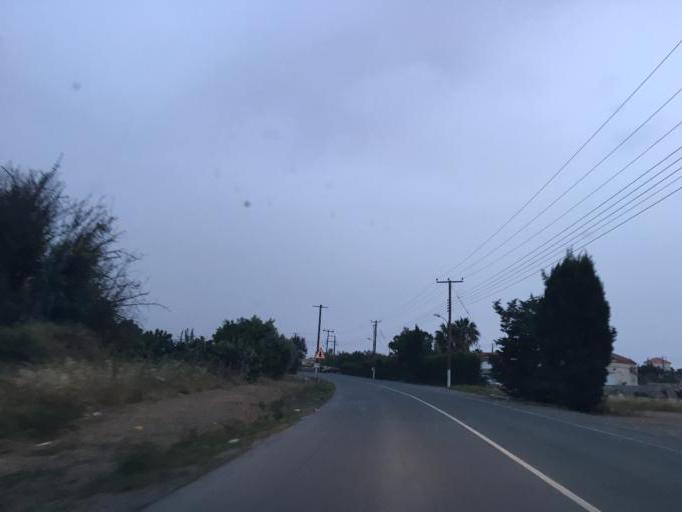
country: CY
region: Limassol
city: Parekklisha
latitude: 34.7443
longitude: 33.1554
